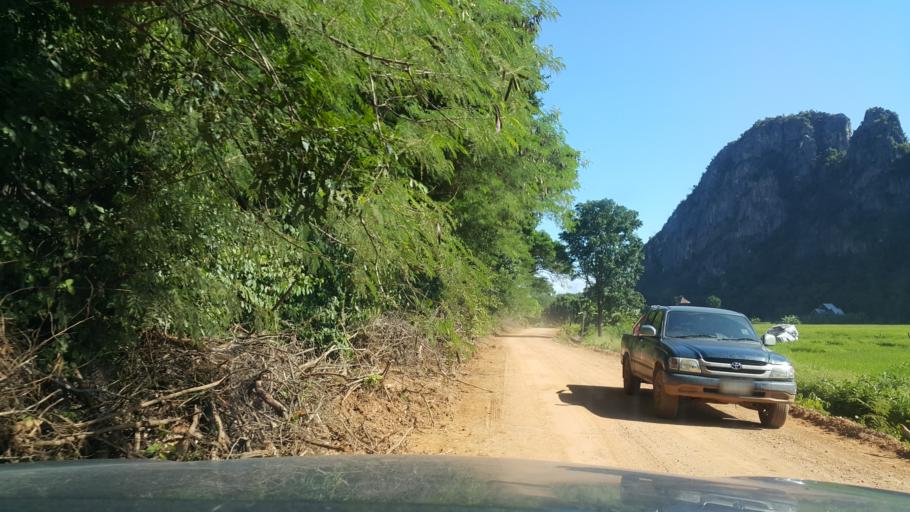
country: TH
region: Sukhothai
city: Thung Saliam
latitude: 17.3303
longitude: 99.5060
